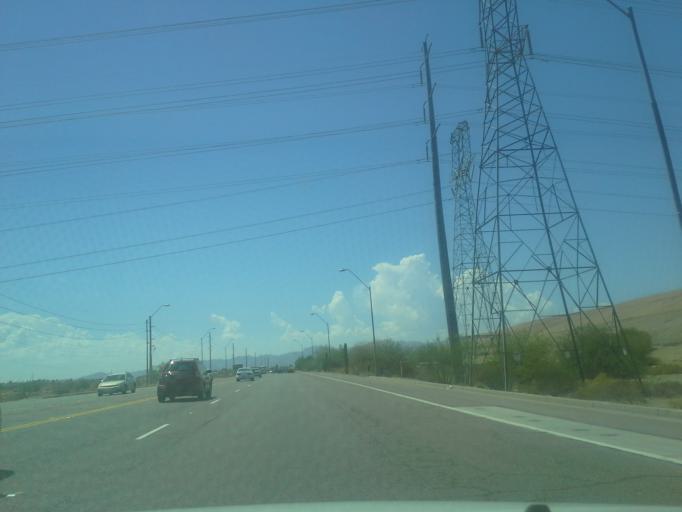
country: US
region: Arizona
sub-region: Maricopa County
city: Youngtown
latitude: 33.5365
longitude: -112.2976
